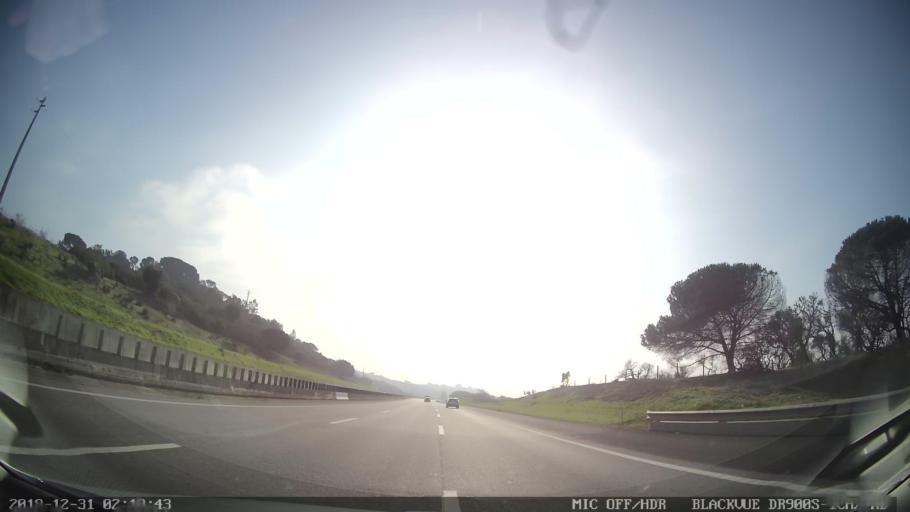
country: PT
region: Lisbon
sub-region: Alenquer
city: Carregado
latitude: 39.0591
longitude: -8.9412
